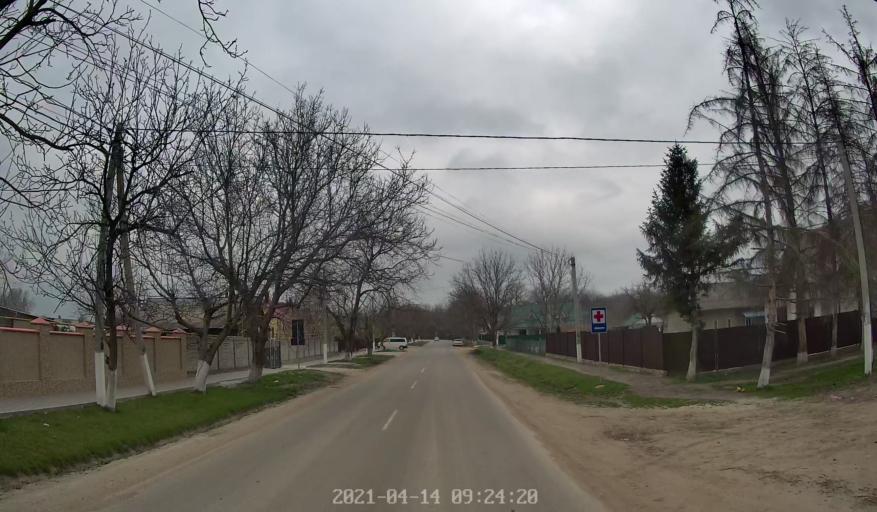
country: MD
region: Chisinau
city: Vadul lui Voda
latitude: 47.1087
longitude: 29.1144
